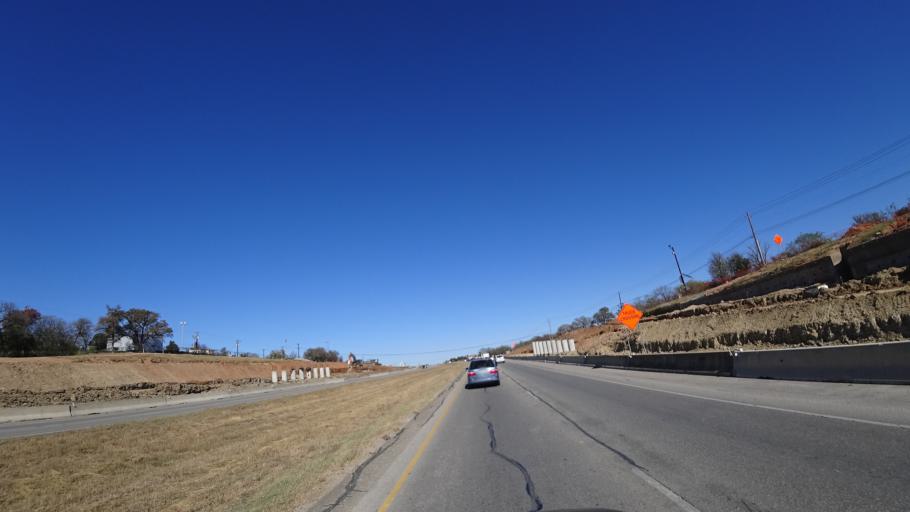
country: US
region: Texas
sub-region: Travis County
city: Austin
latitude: 30.2650
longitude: -97.6716
